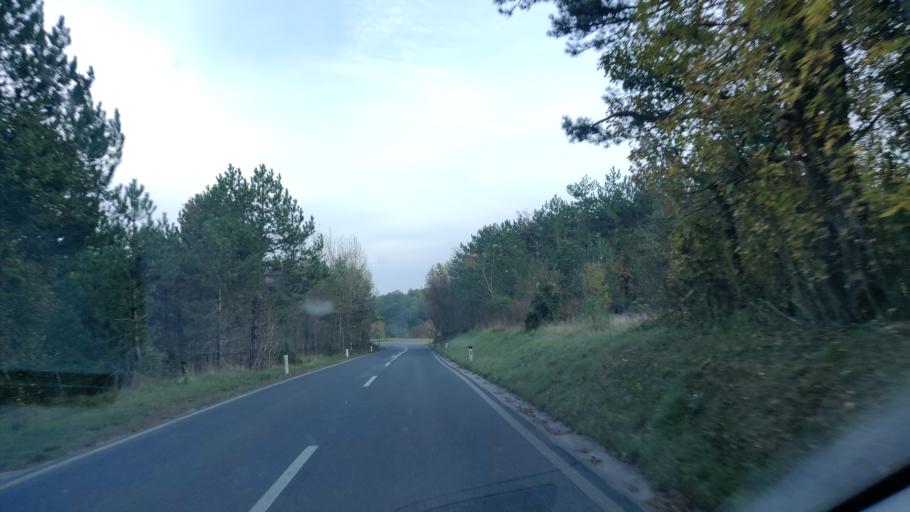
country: SI
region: Komen
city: Komen
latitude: 45.8204
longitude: 13.7548
